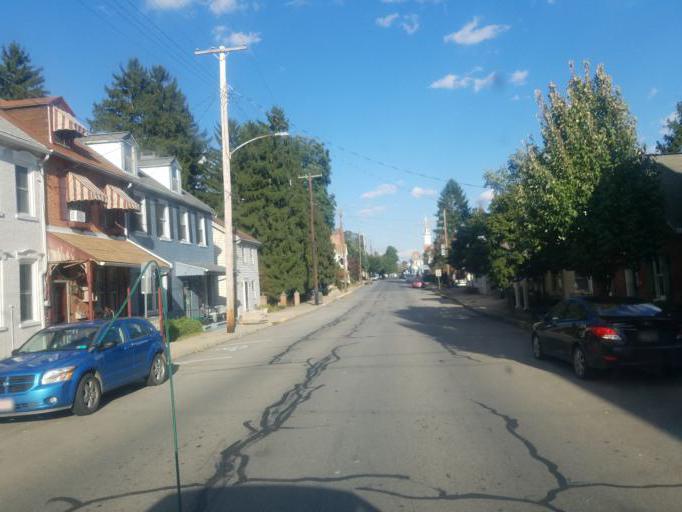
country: US
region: Pennsylvania
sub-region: Lancaster County
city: Marietta
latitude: 40.0574
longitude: -76.5514
